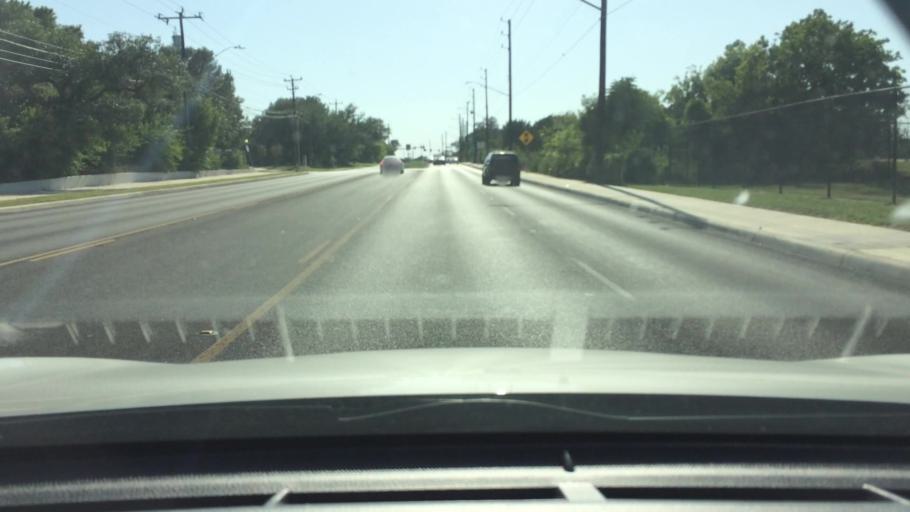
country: US
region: Texas
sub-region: Bexar County
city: Helotes
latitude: 29.5710
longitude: -98.6404
